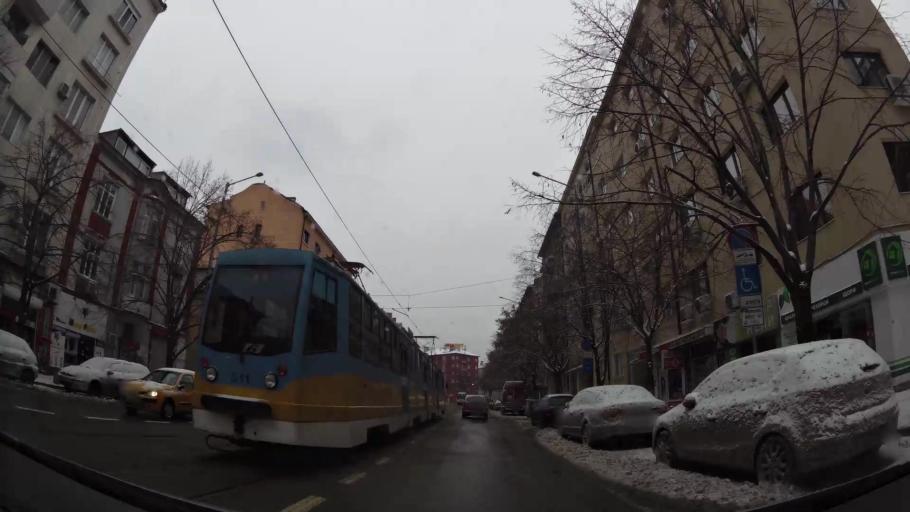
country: BG
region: Sofia-Capital
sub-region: Stolichna Obshtina
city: Sofia
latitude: 42.6909
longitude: 23.3143
